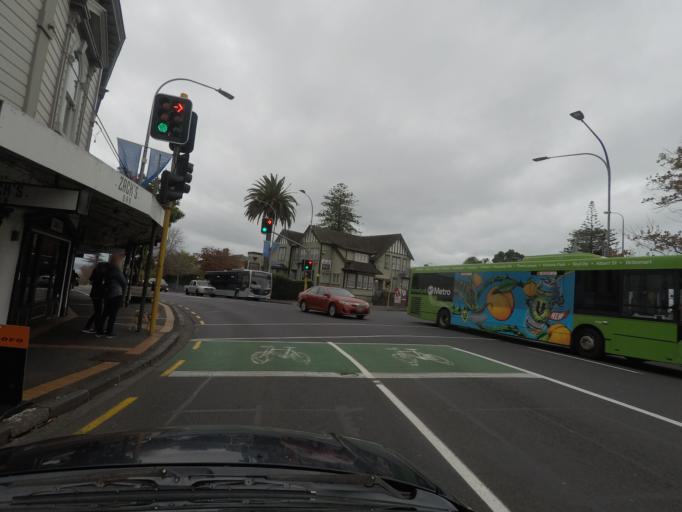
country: NZ
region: Auckland
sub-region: Auckland
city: Auckland
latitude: -36.8590
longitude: 174.7831
